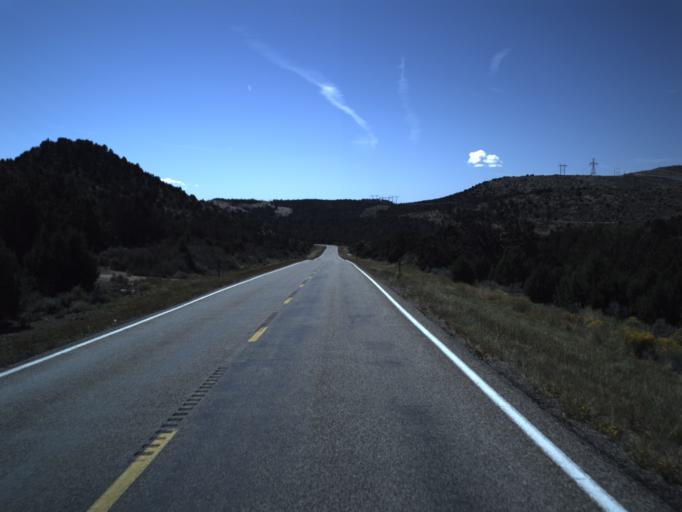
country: US
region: Utah
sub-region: Washington County
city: Enterprise
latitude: 37.4450
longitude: -113.6252
